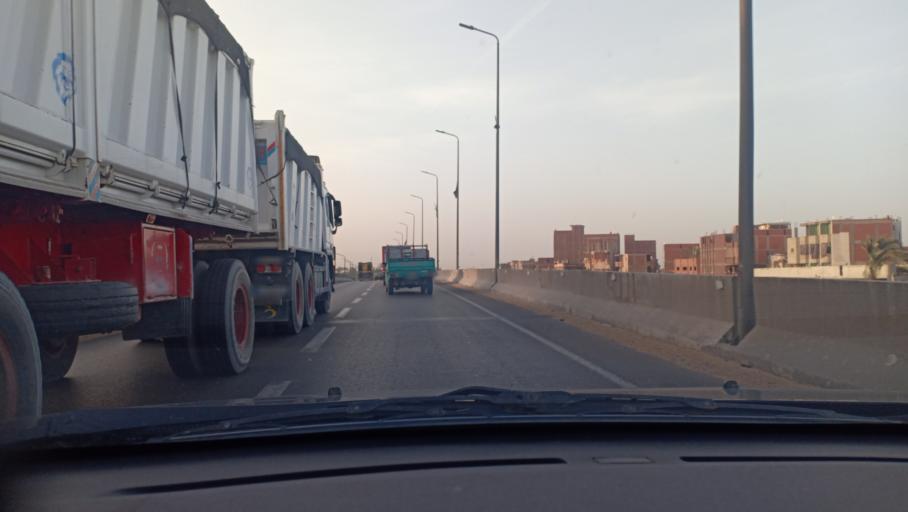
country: EG
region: Muhafazat al Minufiyah
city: Quwaysina
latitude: 30.5483
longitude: 31.2691
